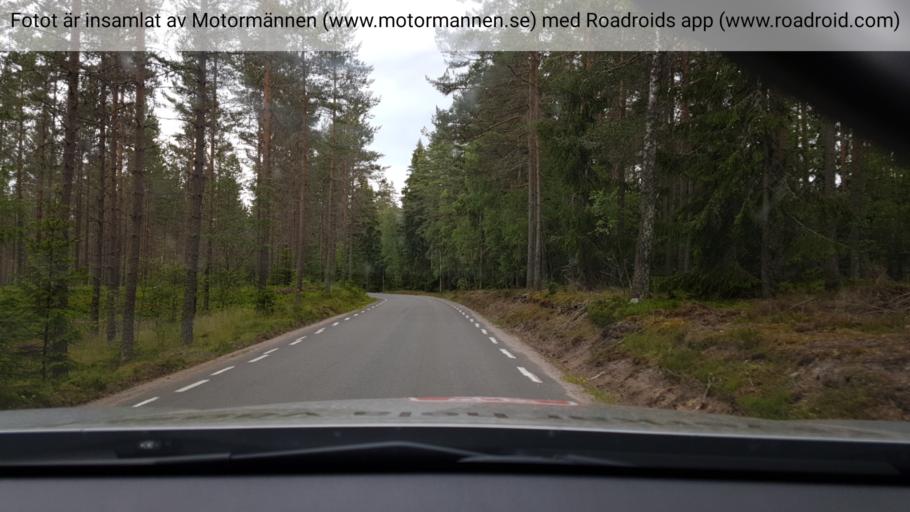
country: SE
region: Vaestra Goetaland
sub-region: Tidaholms Kommun
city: Tidaholm
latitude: 58.0727
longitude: 14.0674
